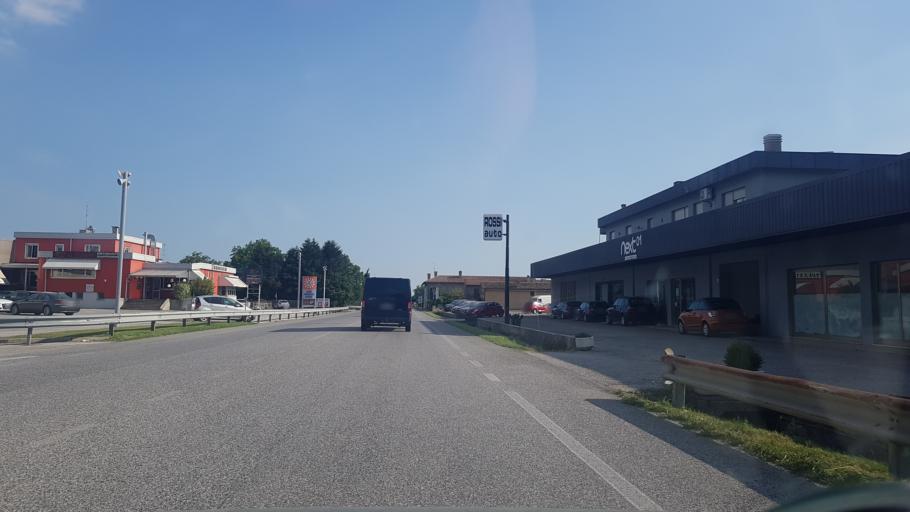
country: IT
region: Friuli Venezia Giulia
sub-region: Provincia di Udine
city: Gemona
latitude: 46.2765
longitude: 13.1088
